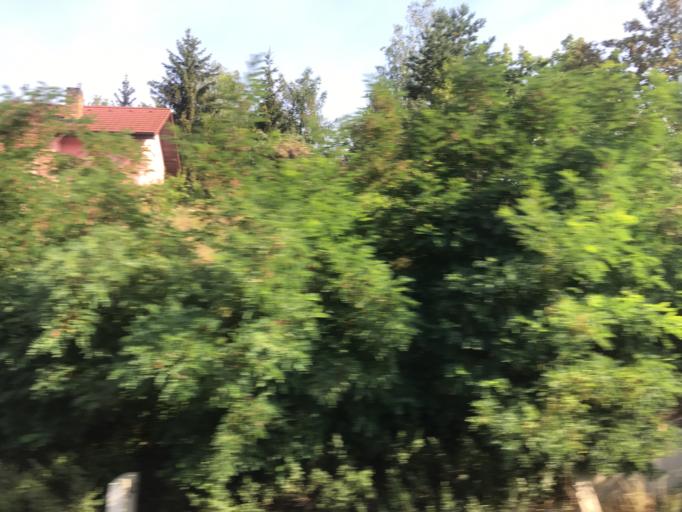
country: CZ
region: Jihocesky
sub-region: Okres Tabor
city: Tabor
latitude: 49.4330
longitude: 14.6695
